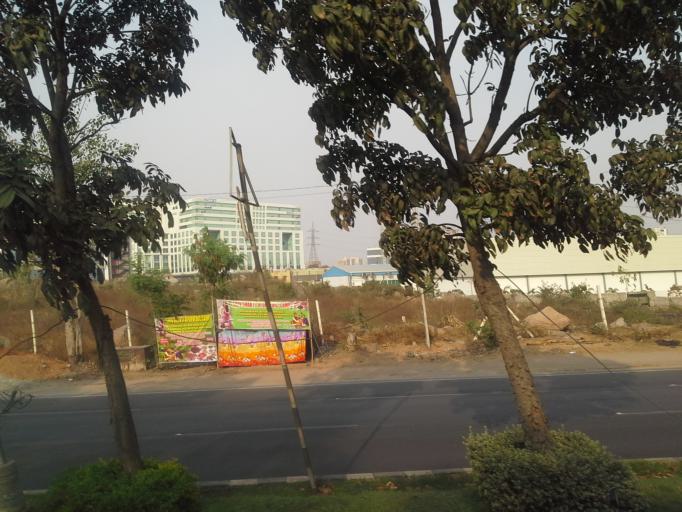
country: IN
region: Telangana
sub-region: Medak
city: Serilingampalle
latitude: 17.4437
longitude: 78.3543
